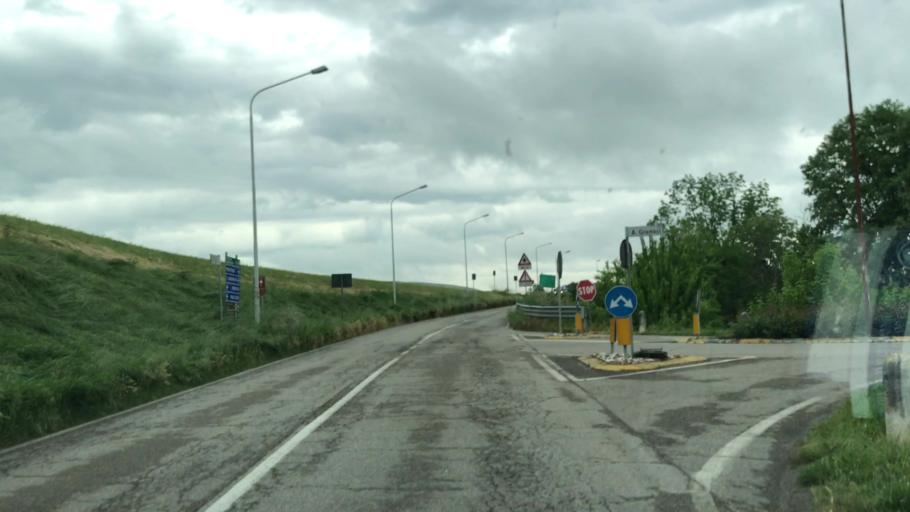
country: IT
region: Lombardy
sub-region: Provincia di Mantova
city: Quistello
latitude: 45.0067
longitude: 10.9770
